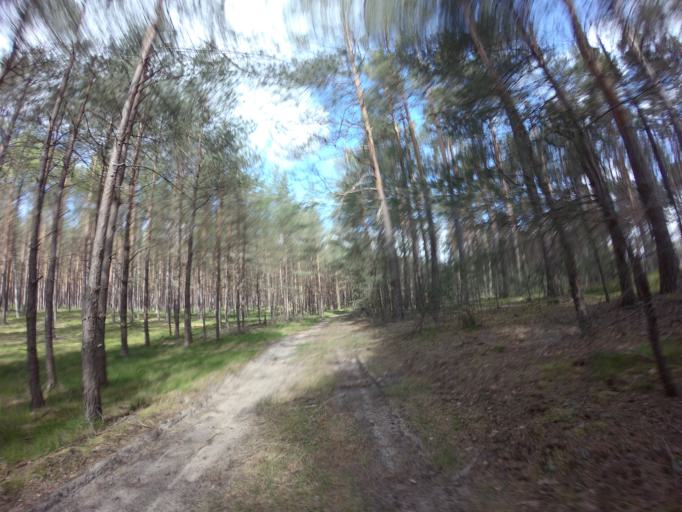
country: PL
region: West Pomeranian Voivodeship
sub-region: Powiat drawski
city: Kalisz Pomorski
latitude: 53.1950
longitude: 15.9989
